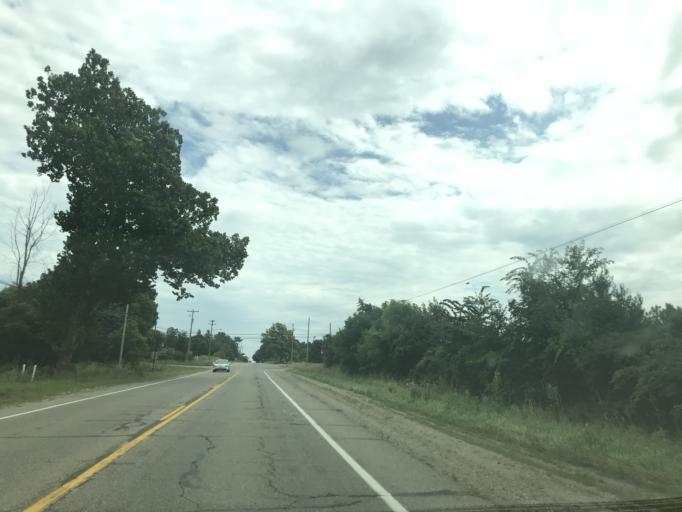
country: US
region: Michigan
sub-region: Clinton County
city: Wacousta
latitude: 42.7911
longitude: -84.7023
